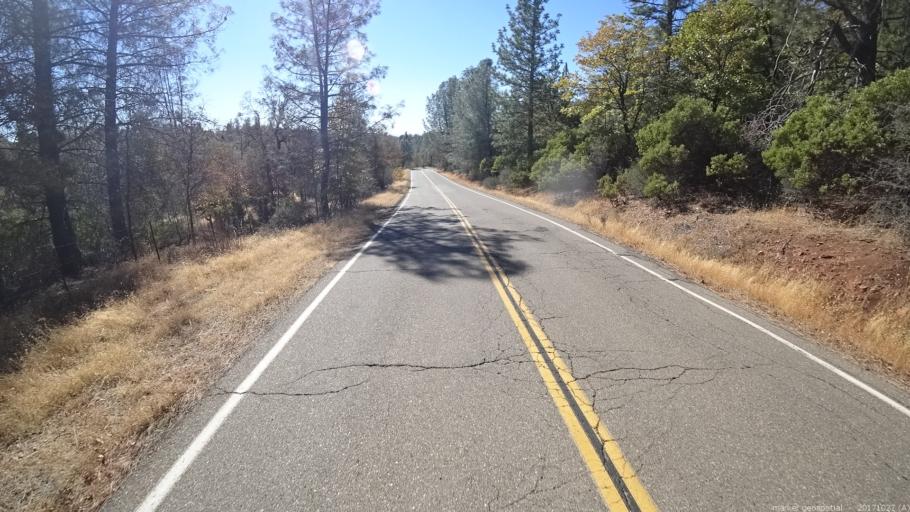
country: US
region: California
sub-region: Shasta County
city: Shingletown
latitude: 40.7076
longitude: -121.9741
